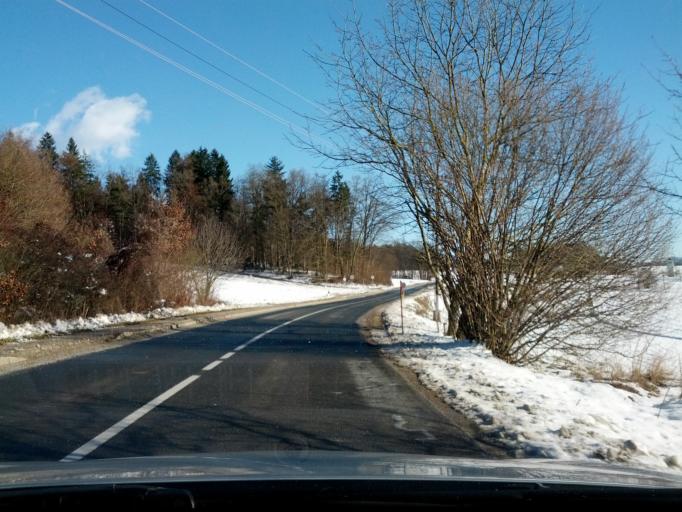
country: SI
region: Lukovica
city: Lukovica pri Domzalah
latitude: 46.1389
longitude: 14.7059
